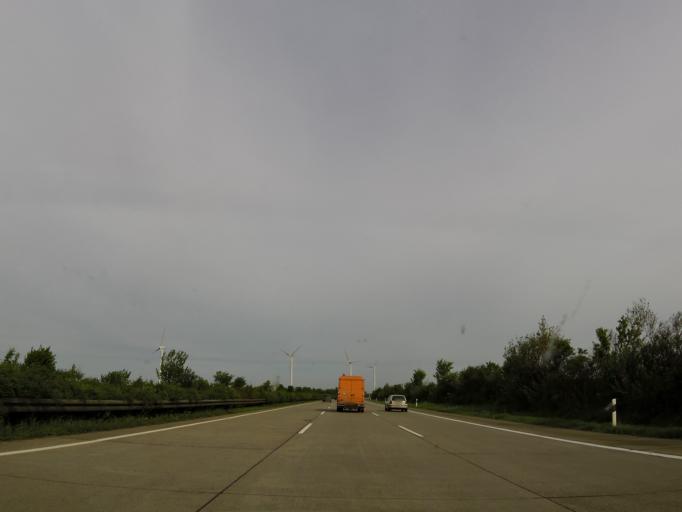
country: DE
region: Lower Saxony
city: Harsum
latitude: 52.1947
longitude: 9.9494
